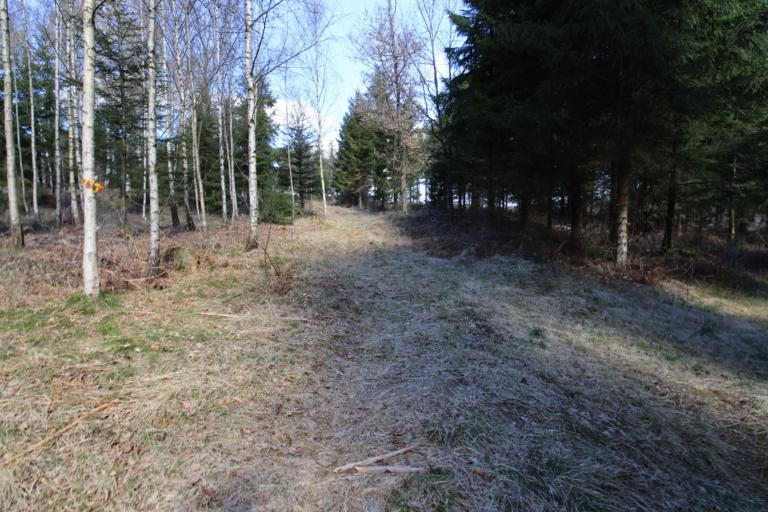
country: SE
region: Halland
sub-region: Varbergs Kommun
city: Varberg
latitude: 57.1917
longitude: 12.2363
